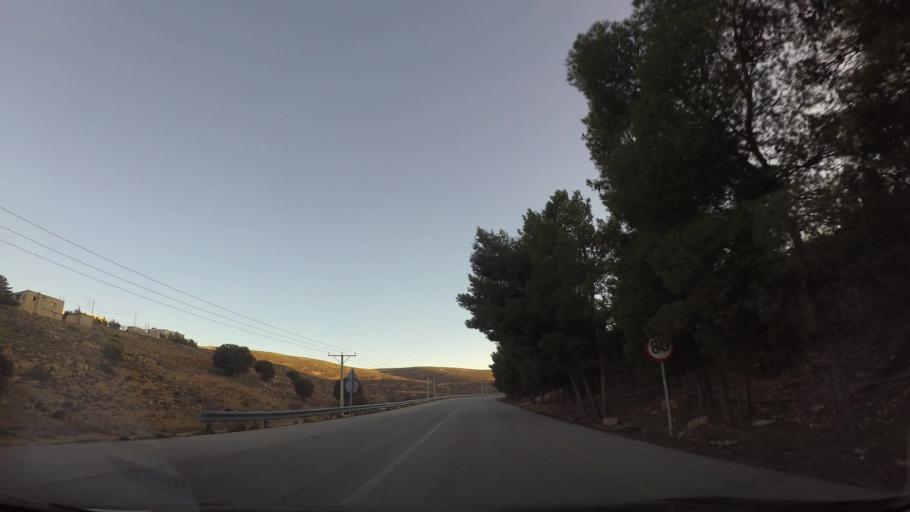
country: JO
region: Ma'an
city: Petra
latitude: 30.4138
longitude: 35.5080
